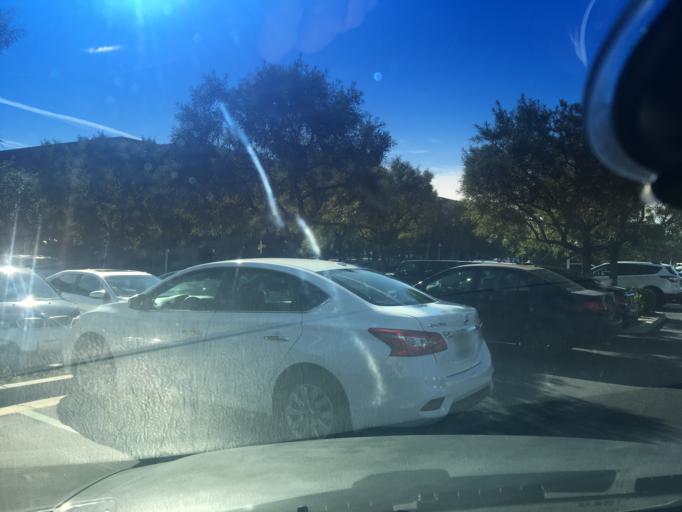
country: US
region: California
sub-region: Orange County
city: San Joaquin Hills
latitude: 33.6098
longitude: -117.8794
